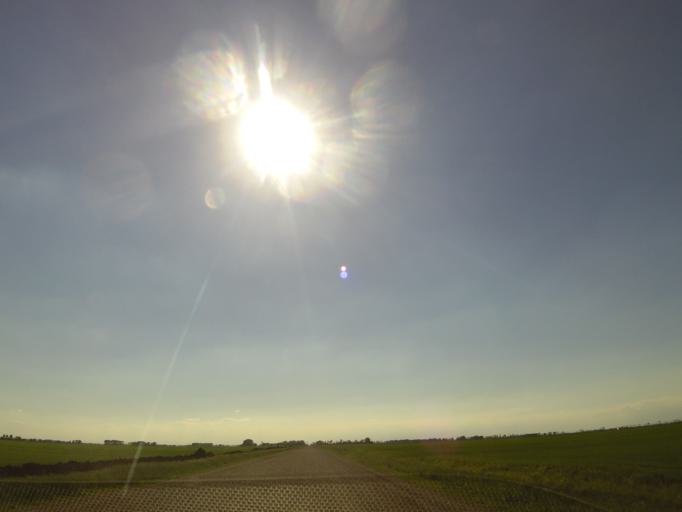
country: US
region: North Dakota
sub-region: Walsh County
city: Grafton
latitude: 48.3684
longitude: -97.2689
